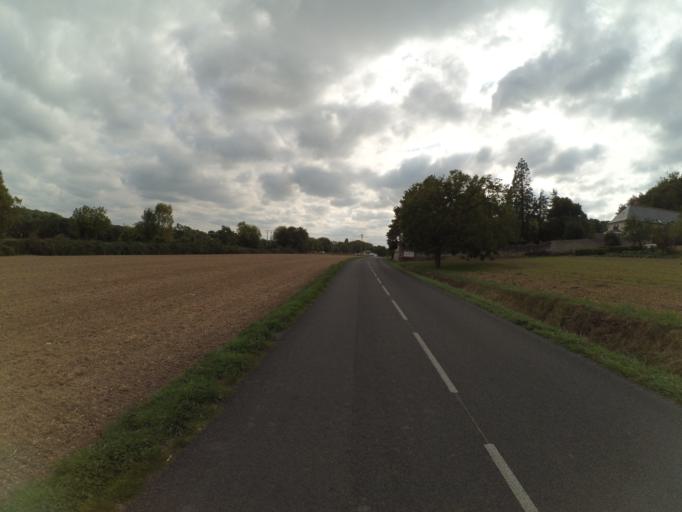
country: FR
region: Centre
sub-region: Departement d'Indre-et-Loire
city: Reugny
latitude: 47.4632
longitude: 0.8791
